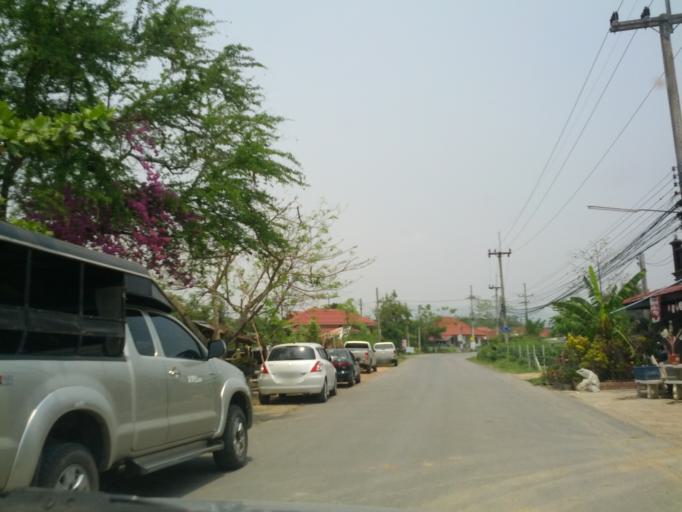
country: TH
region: Chiang Mai
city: San Sai
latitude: 18.9001
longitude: 99.0347
